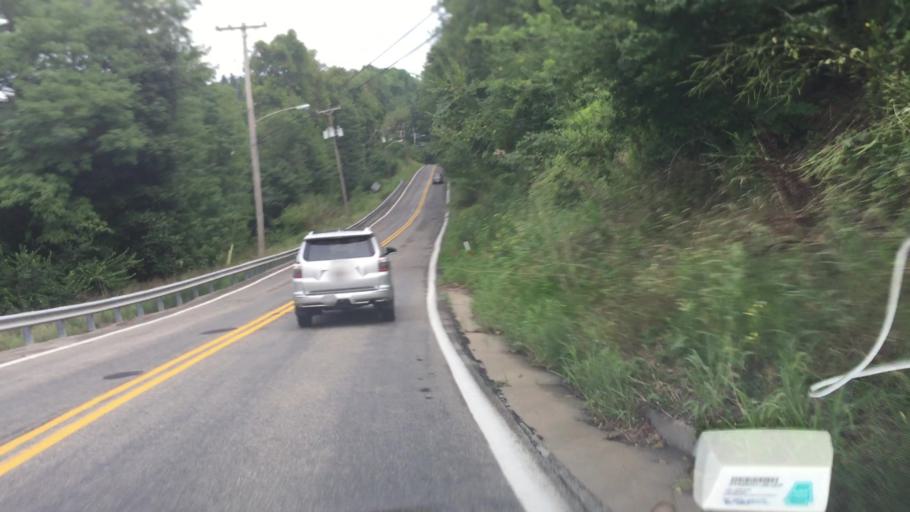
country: US
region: Pennsylvania
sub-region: Allegheny County
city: Heidelberg
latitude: 40.3820
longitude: -80.0902
